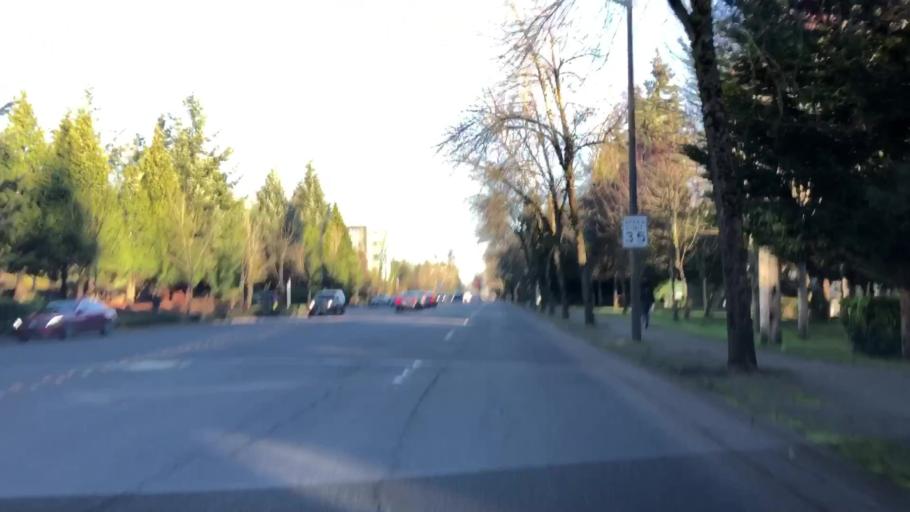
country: US
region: Washington
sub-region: King County
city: Redmond
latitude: 47.6469
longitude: -122.1322
